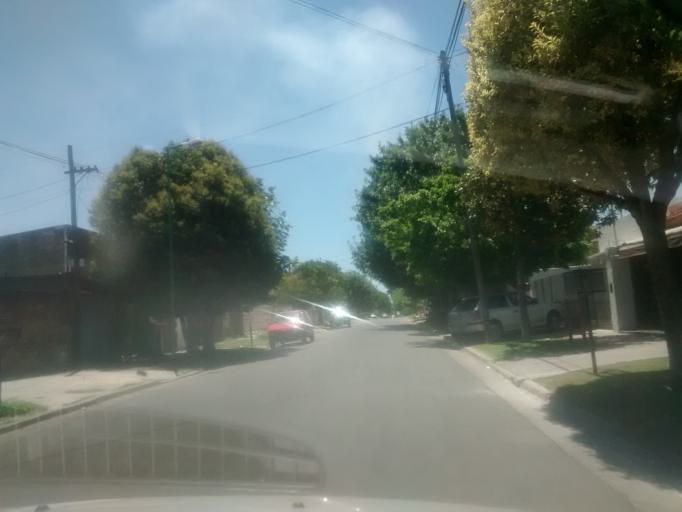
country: AR
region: Buenos Aires
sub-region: Partido de La Plata
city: La Plata
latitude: -34.9428
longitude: -57.9320
